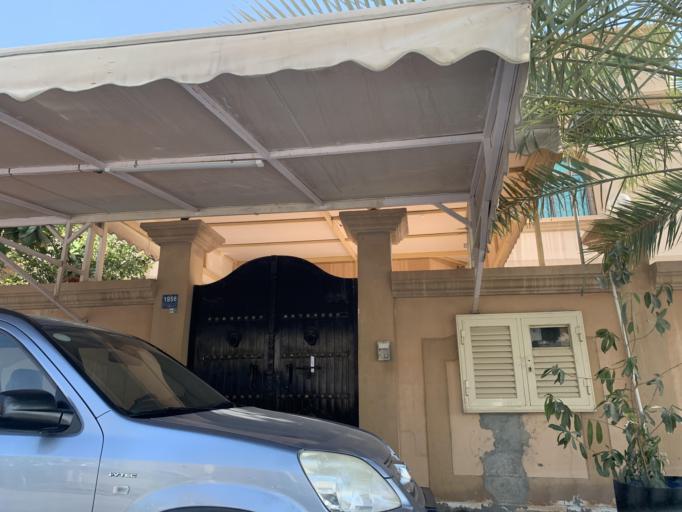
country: BH
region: Manama
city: Jidd Hafs
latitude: 26.1967
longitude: 50.5172
